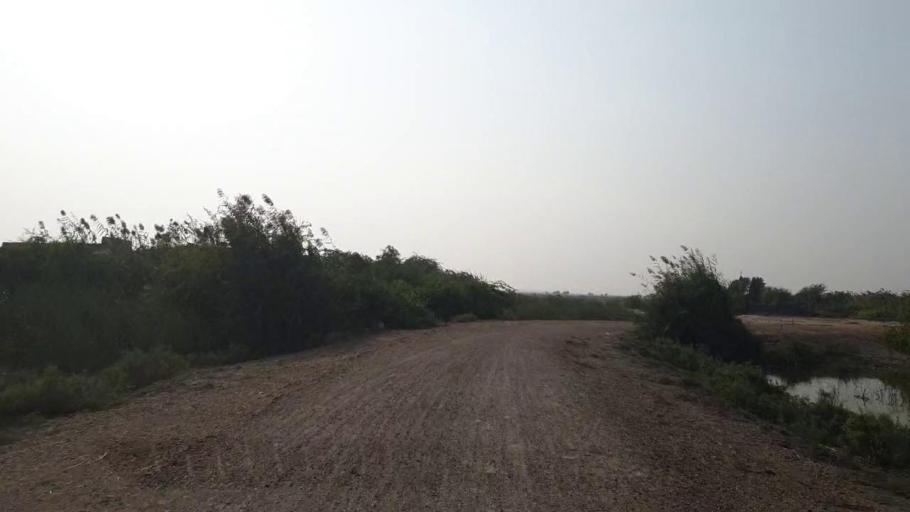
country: PK
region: Sindh
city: Tando Muhammad Khan
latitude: 25.0809
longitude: 68.3398
